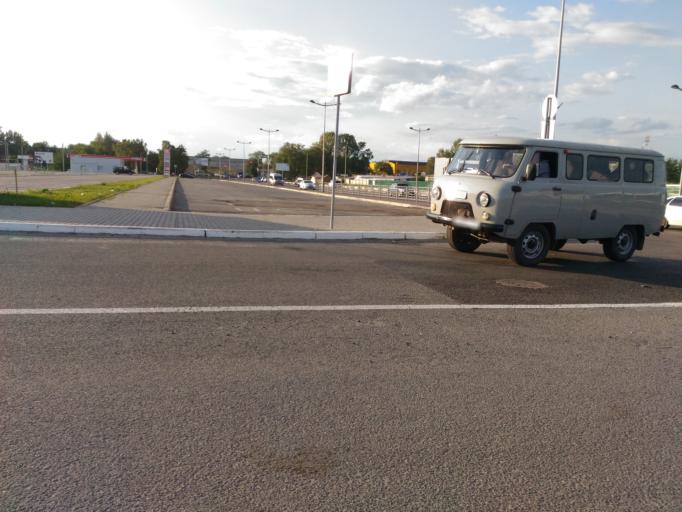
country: RU
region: Ulyanovsk
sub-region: Ulyanovskiy Rayon
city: Ulyanovsk
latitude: 54.2915
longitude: 48.2714
